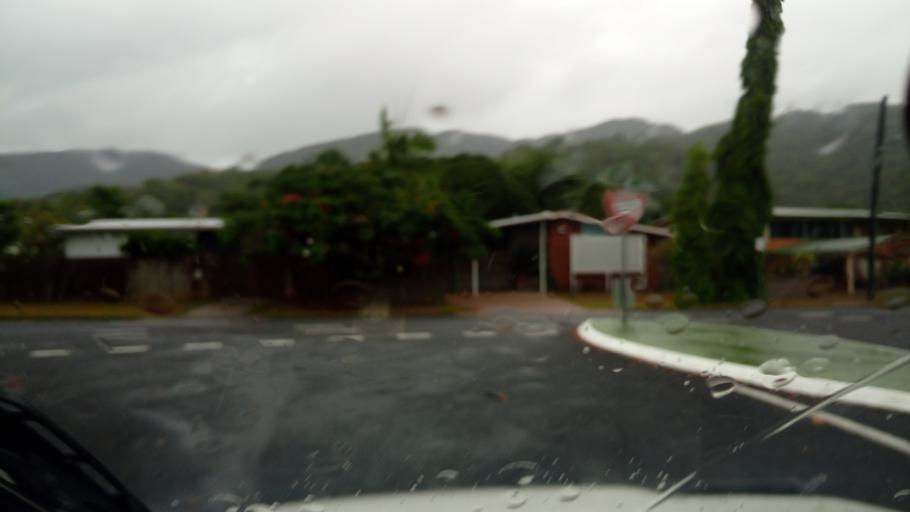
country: AU
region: Queensland
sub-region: Cairns
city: Woree
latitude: -16.9439
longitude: 145.7298
